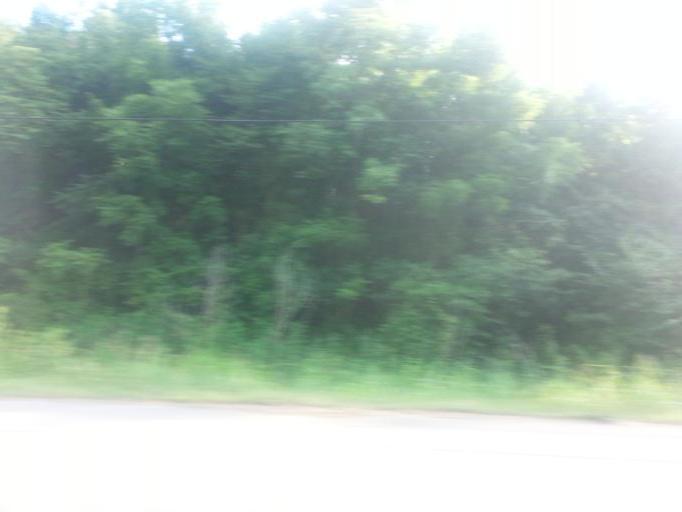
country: US
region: Tennessee
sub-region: Sevier County
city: Sevierville
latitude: 35.8534
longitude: -83.6412
